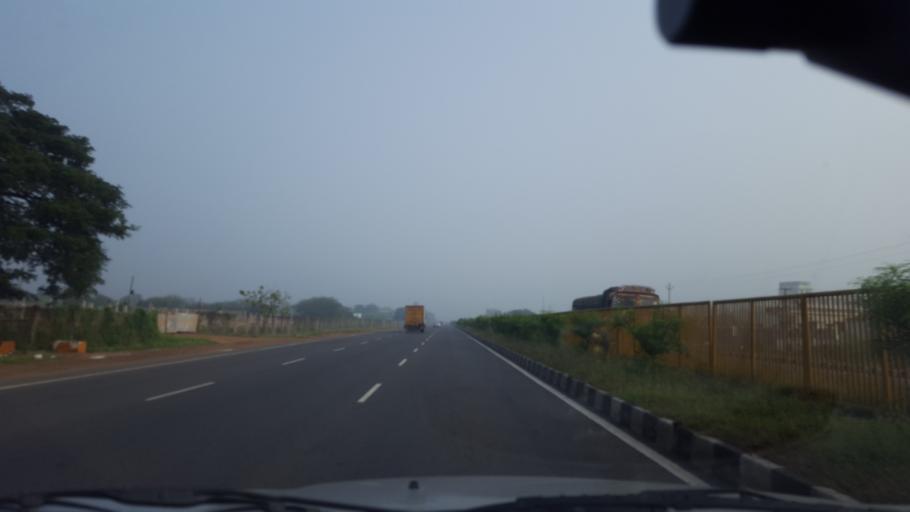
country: IN
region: Andhra Pradesh
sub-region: Prakasam
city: Ongole
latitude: 15.4322
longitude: 80.0432
